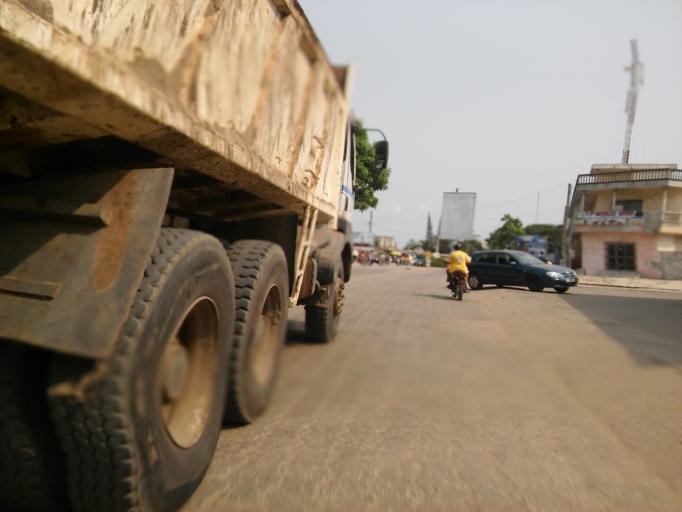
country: BJ
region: Littoral
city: Cotonou
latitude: 6.3903
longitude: 2.4006
